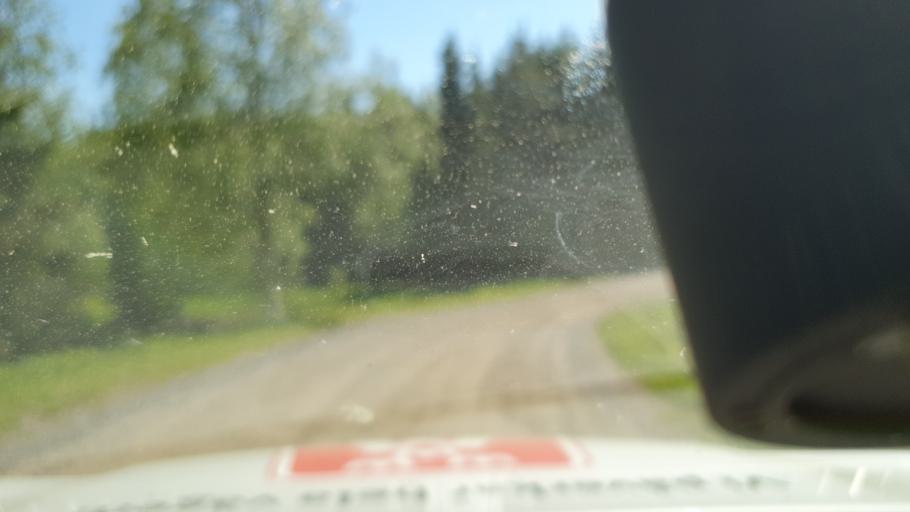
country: SE
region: Vaesterbotten
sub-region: Robertsfors Kommun
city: Robertsfors
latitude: 64.3745
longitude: 20.9976
